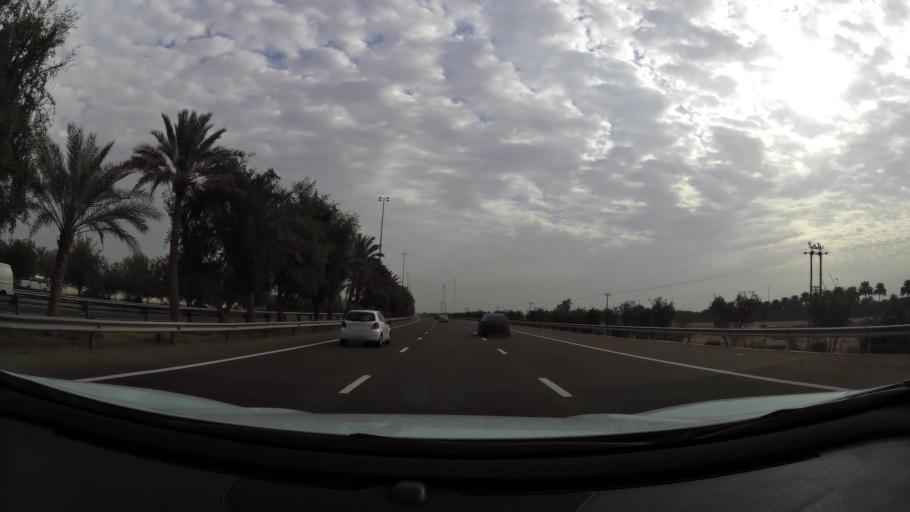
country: AE
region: Abu Dhabi
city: Al Ain
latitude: 24.1852
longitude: 55.3407
